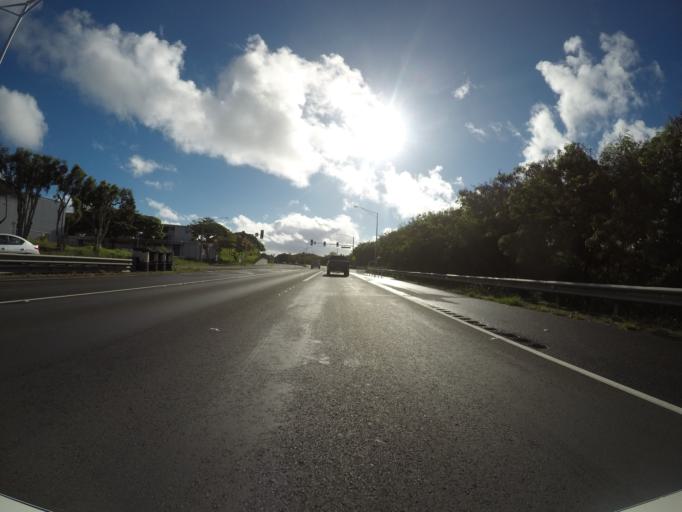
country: US
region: Hawaii
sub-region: Honolulu County
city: Kailua
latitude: 21.4066
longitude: -157.7587
